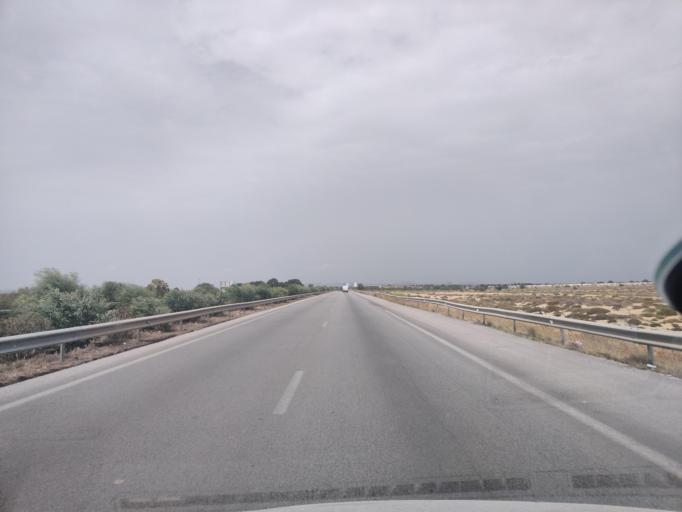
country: TN
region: Susah
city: Harqalah
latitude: 36.0734
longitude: 10.4046
